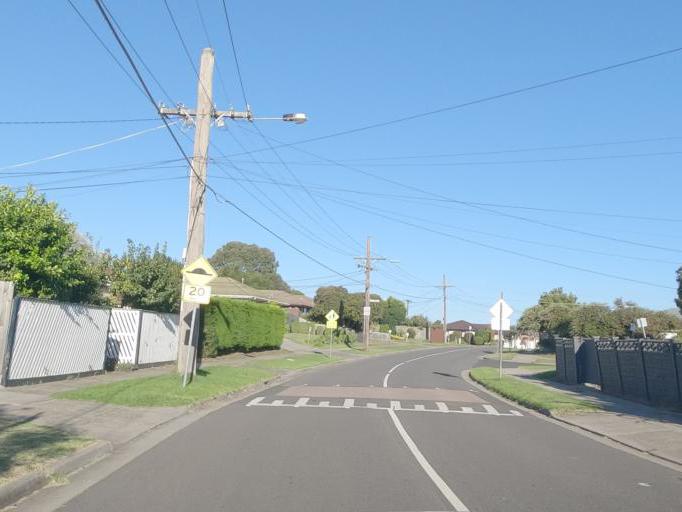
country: AU
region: Victoria
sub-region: Hume
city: Gladstone Park
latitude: -37.6867
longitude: 144.8915
